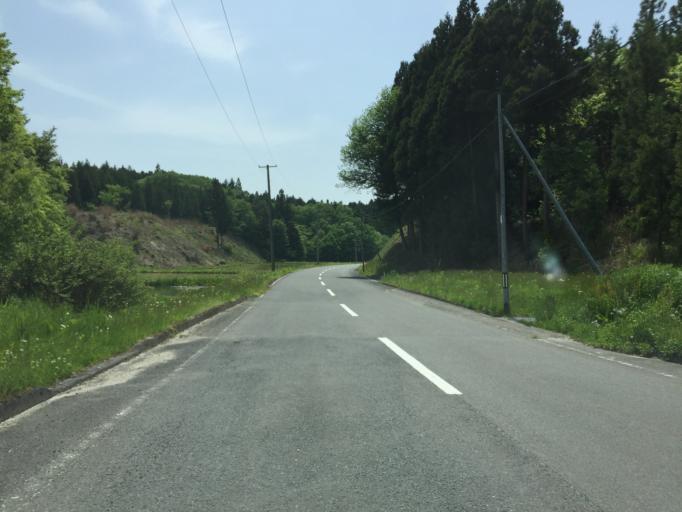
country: JP
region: Fukushima
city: Ishikawa
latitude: 37.1845
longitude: 140.5320
